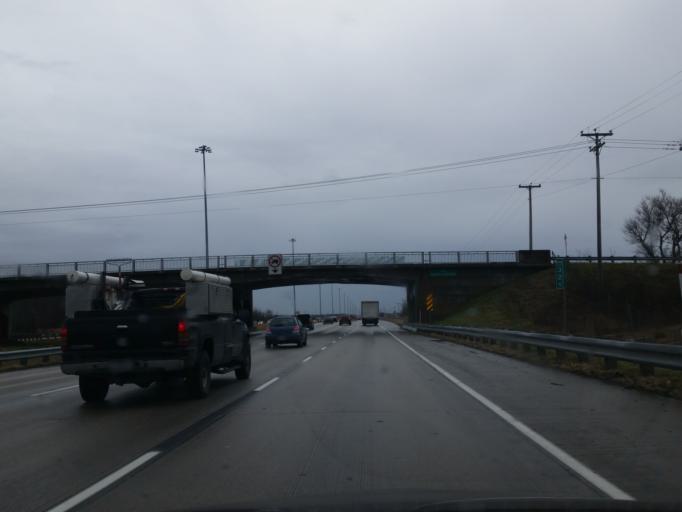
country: CA
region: Quebec
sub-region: Laurentides
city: Blainville
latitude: 45.7050
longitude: -73.9565
